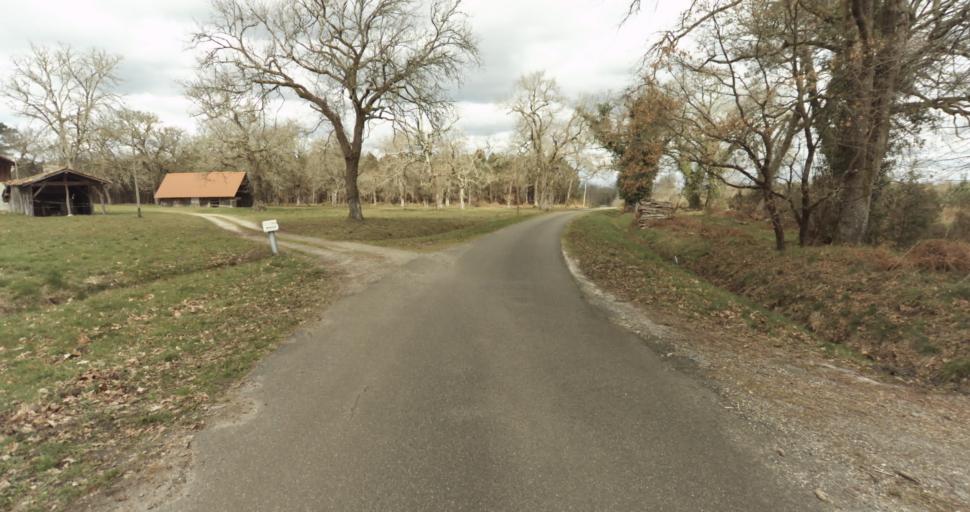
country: FR
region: Aquitaine
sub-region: Departement des Landes
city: Roquefort
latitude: 44.0910
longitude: -0.4545
